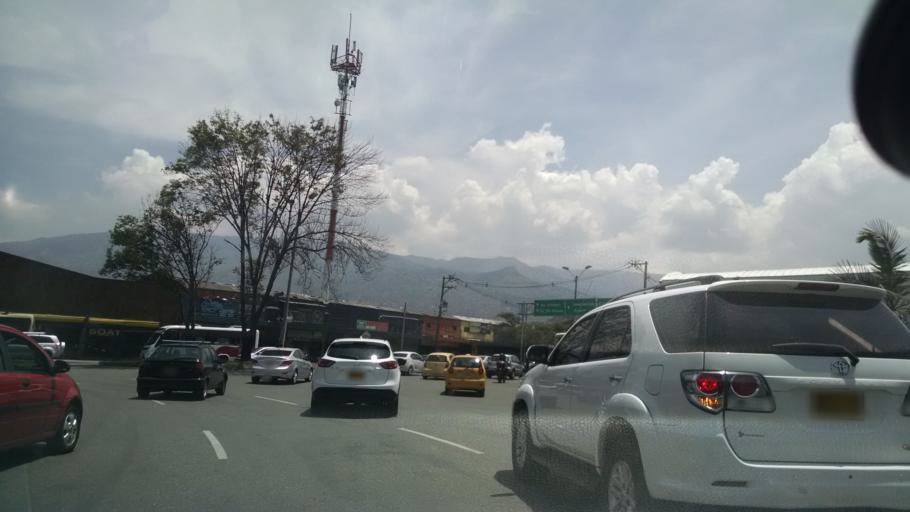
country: CO
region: Antioquia
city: Medellin
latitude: 6.2390
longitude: -75.5753
